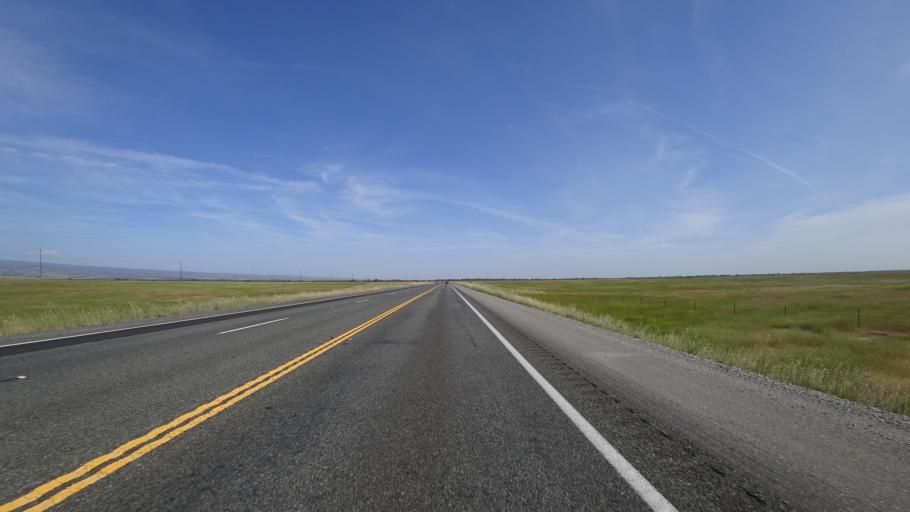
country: US
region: California
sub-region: Tehama County
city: Los Molinos
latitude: 39.9055
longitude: -122.0029
